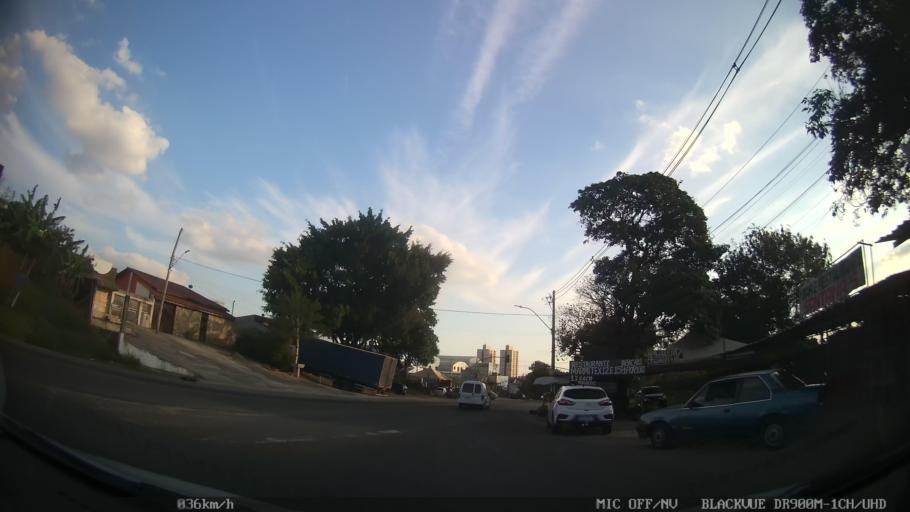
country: BR
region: Sao Paulo
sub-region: Hortolandia
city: Hortolandia
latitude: -22.8856
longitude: -47.1622
